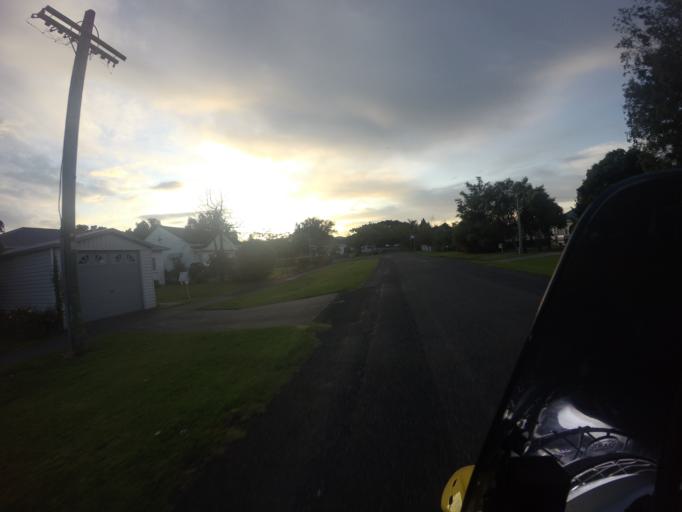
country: NZ
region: Gisborne
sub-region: Gisborne District
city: Gisborne
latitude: -38.6648
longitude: 178.0363
